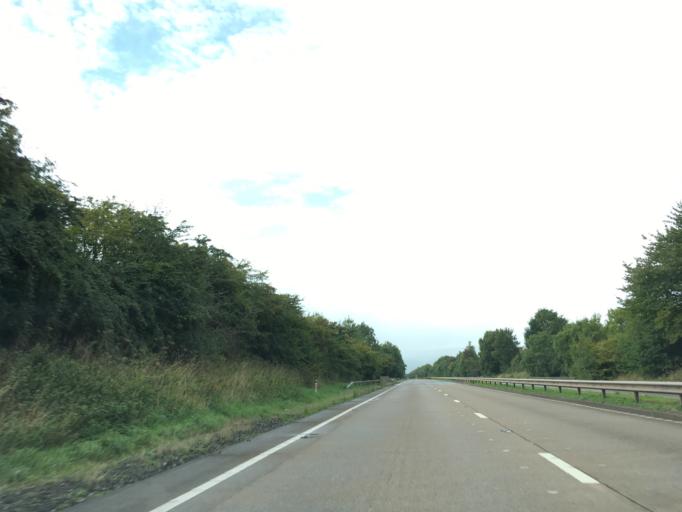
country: GB
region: Wales
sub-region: Monmouthshire
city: Llanarth
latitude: 51.7830
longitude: -2.9324
